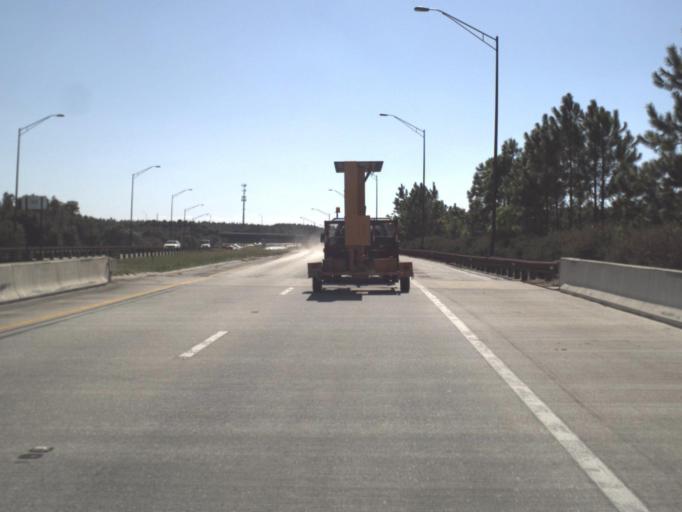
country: US
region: Florida
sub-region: Hillsborough County
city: Greater Northdale
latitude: 28.1286
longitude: -82.5484
